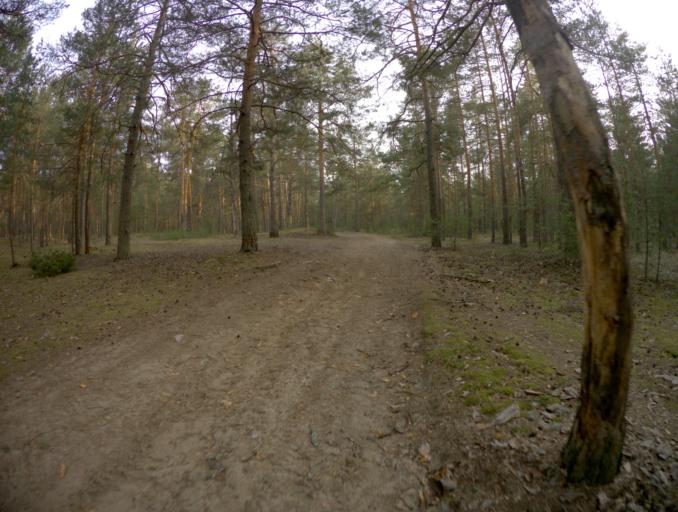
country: RU
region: Vladimir
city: Kommunar
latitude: 56.0837
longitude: 40.4370
